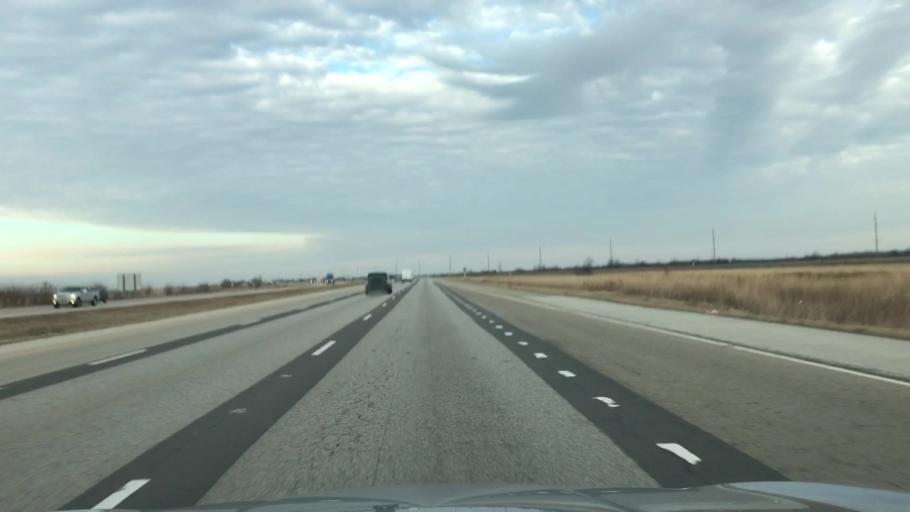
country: US
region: Illinois
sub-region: Logan County
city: Lincoln
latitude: 40.0770
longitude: -89.4377
